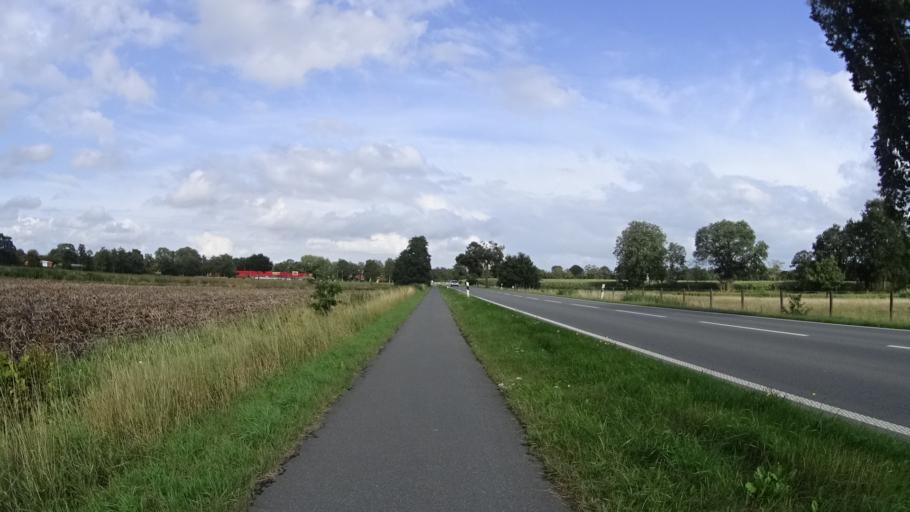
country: DE
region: Lower Saxony
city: Bockhorn
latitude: 53.3887
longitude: 8.0293
